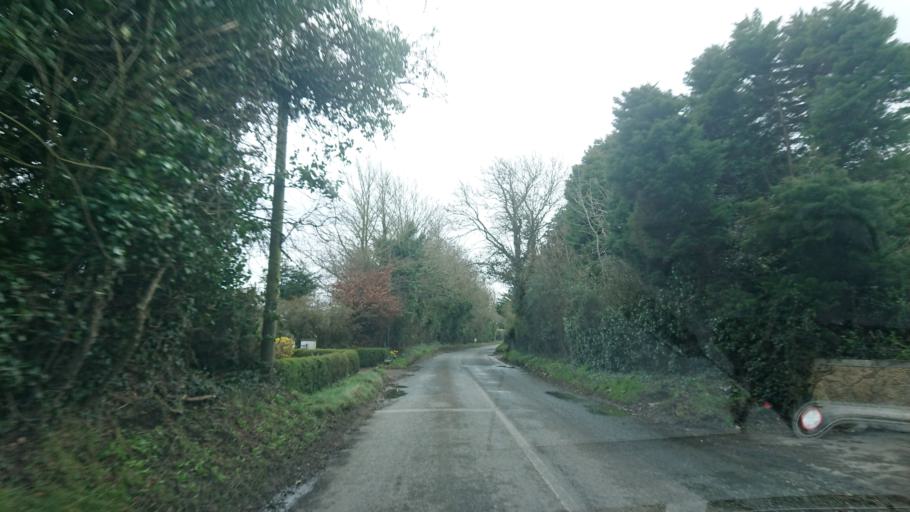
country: IE
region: Leinster
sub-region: Kildare
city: Naas
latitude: 53.1992
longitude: -6.6528
